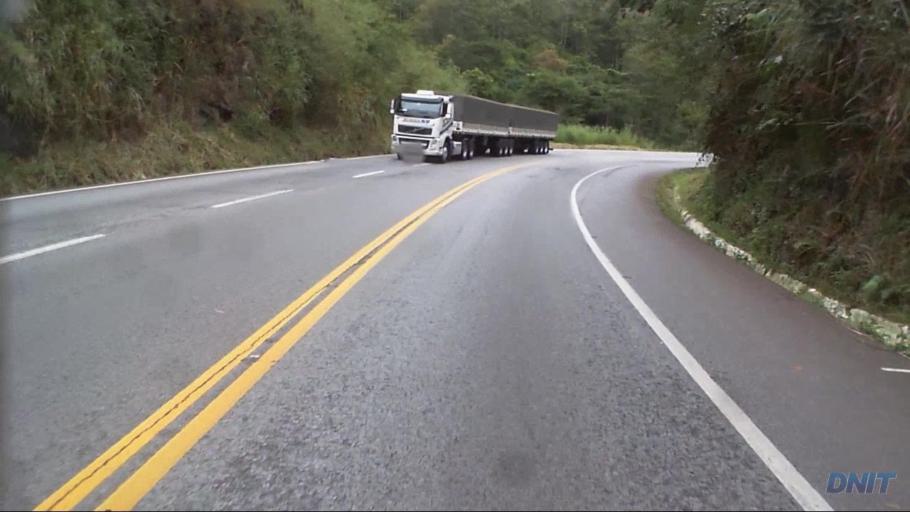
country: BR
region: Minas Gerais
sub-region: Joao Monlevade
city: Joao Monlevade
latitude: -19.8564
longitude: -43.2427
